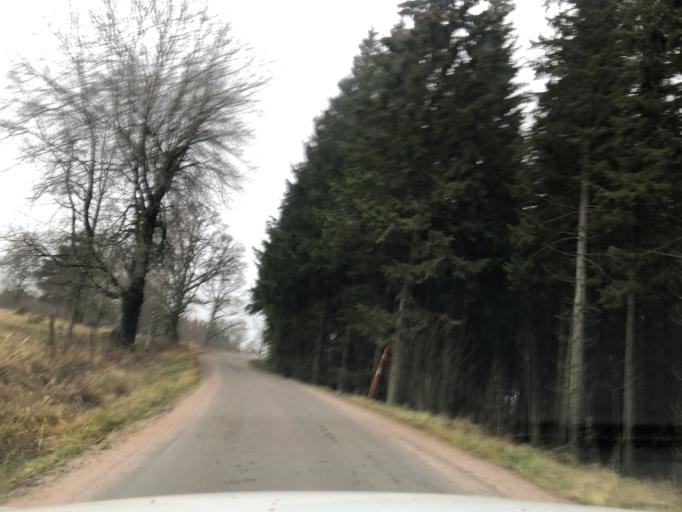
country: SE
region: Vaestra Goetaland
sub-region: Ulricehamns Kommun
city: Ulricehamn
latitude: 57.8489
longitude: 13.6351
